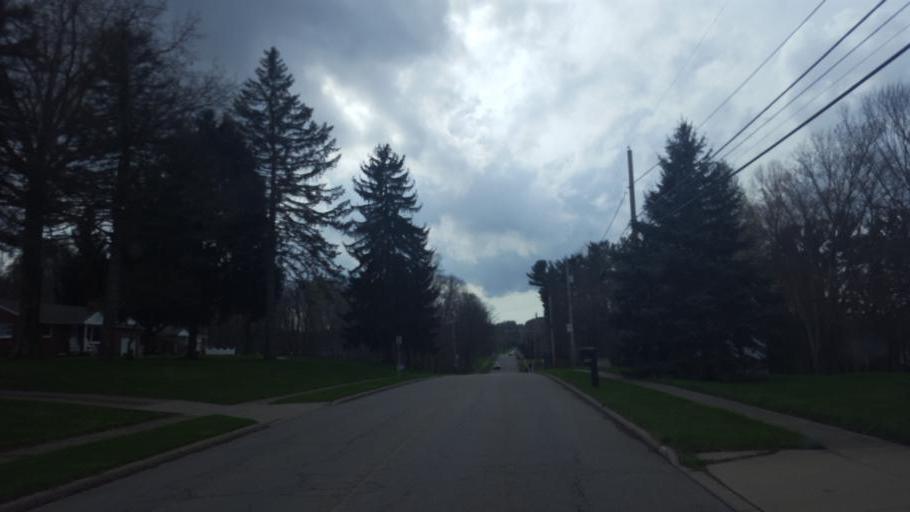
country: US
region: Ohio
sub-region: Richland County
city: Lexington
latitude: 40.6804
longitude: -82.5933
